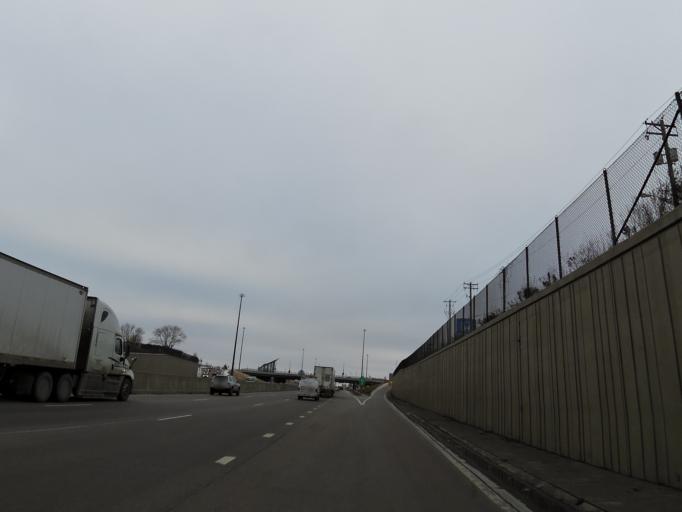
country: US
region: Minnesota
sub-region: Hennepin County
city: Richfield
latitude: 44.8621
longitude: -93.2835
